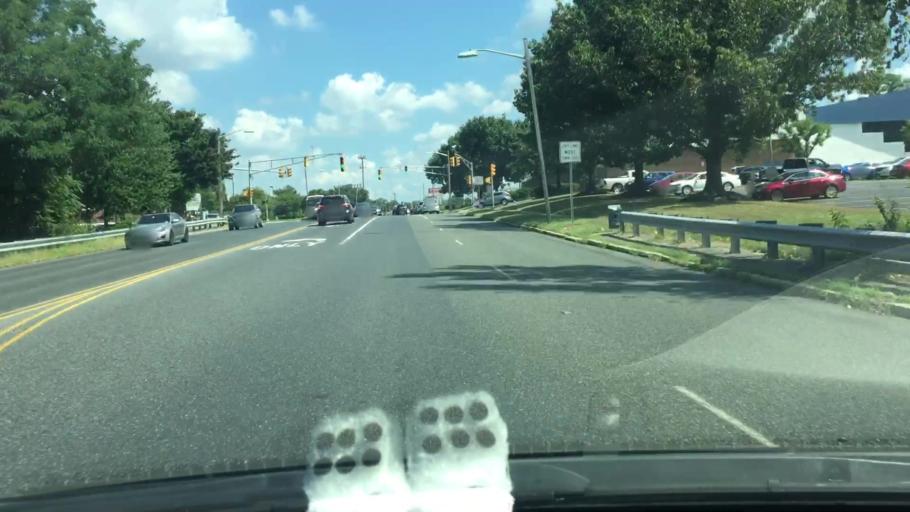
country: US
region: New Jersey
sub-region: Camden County
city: Glendora
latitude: 39.8283
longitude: -75.0945
